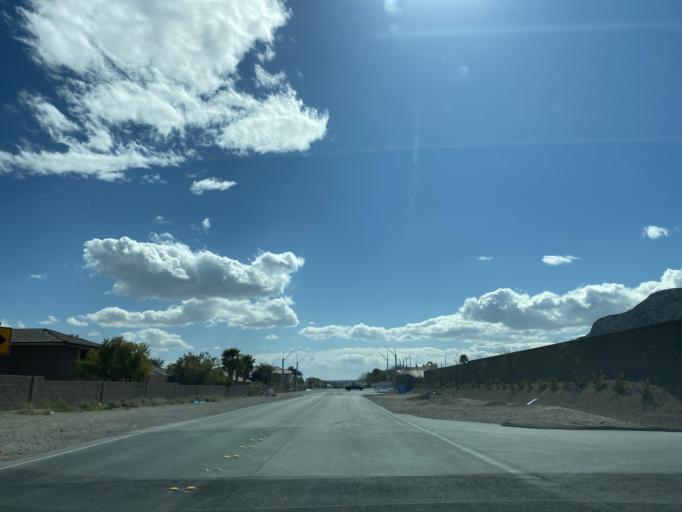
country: US
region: Nevada
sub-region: Clark County
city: Summerlin South
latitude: 36.2495
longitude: -115.3063
